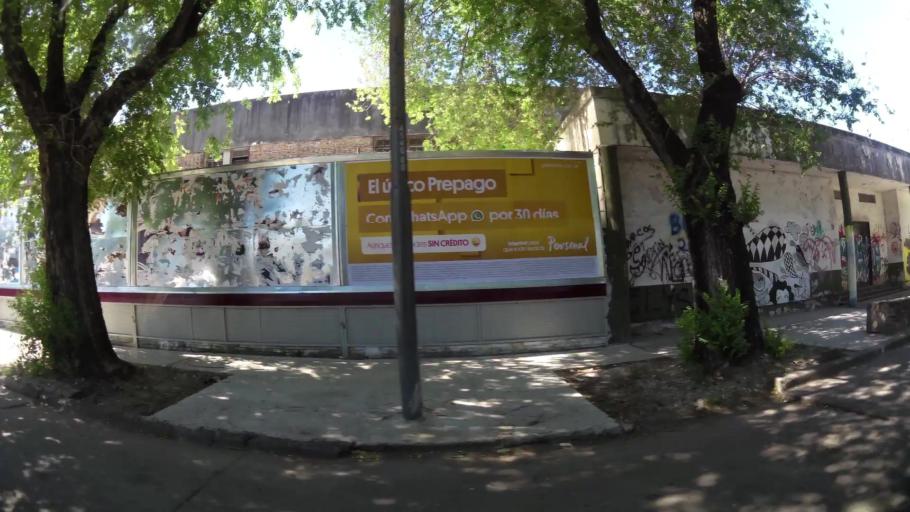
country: AR
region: Santa Fe
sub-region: Departamento de Rosario
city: Rosario
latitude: -32.9356
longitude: -60.6903
